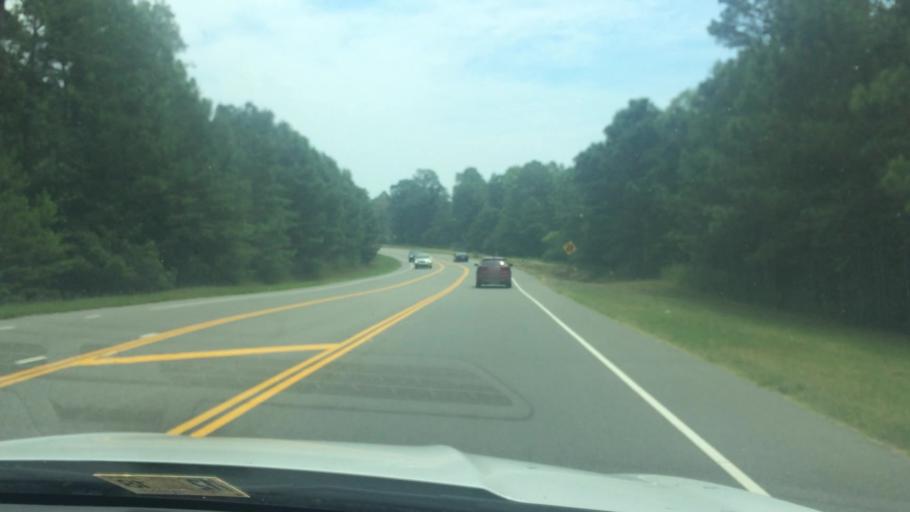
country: US
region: Virginia
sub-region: James City County
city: Williamsburg
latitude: 37.2630
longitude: -76.7876
